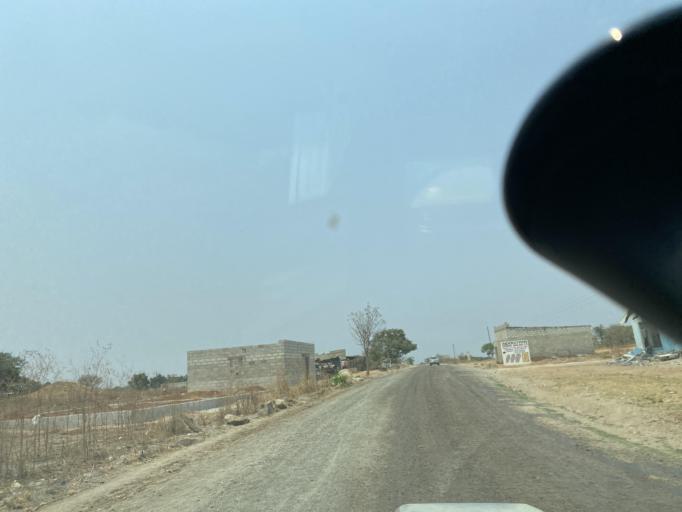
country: ZM
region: Lusaka
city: Lusaka
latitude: -15.5610
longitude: 28.4240
